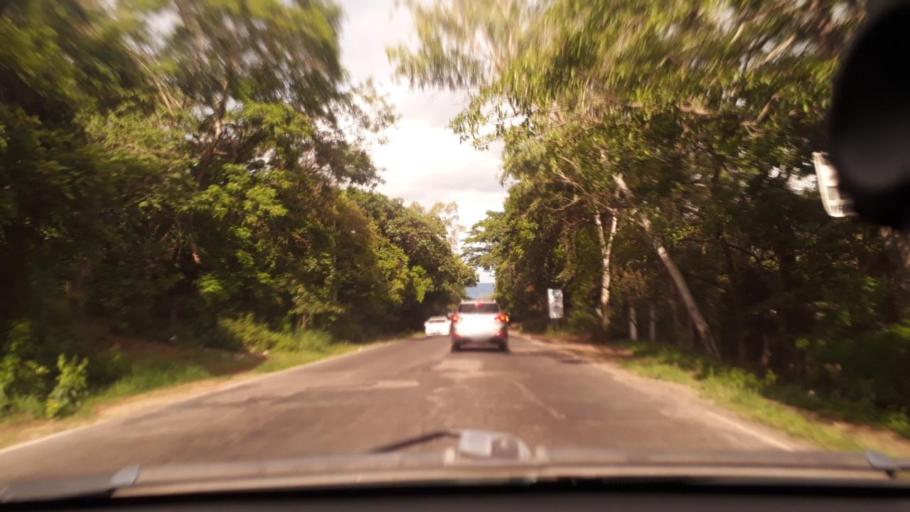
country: GT
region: Jutiapa
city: Quesada
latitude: 14.2755
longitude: -89.9768
